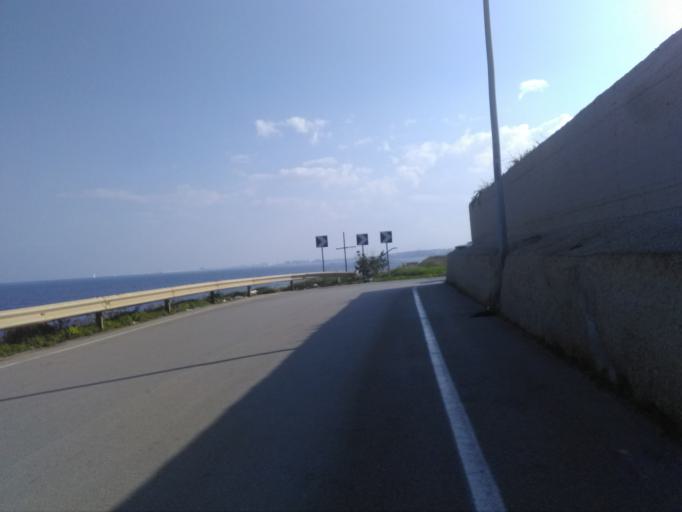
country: IT
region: Apulia
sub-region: Provincia di Bari
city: San Paolo
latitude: 41.1517
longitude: 16.7889
